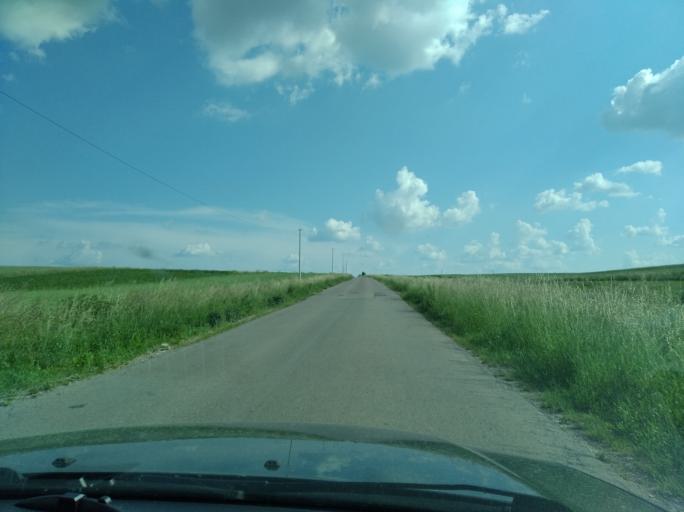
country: PL
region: Subcarpathian Voivodeship
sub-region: Powiat jaroslawski
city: Ostrow
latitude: 49.9361
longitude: 22.7399
